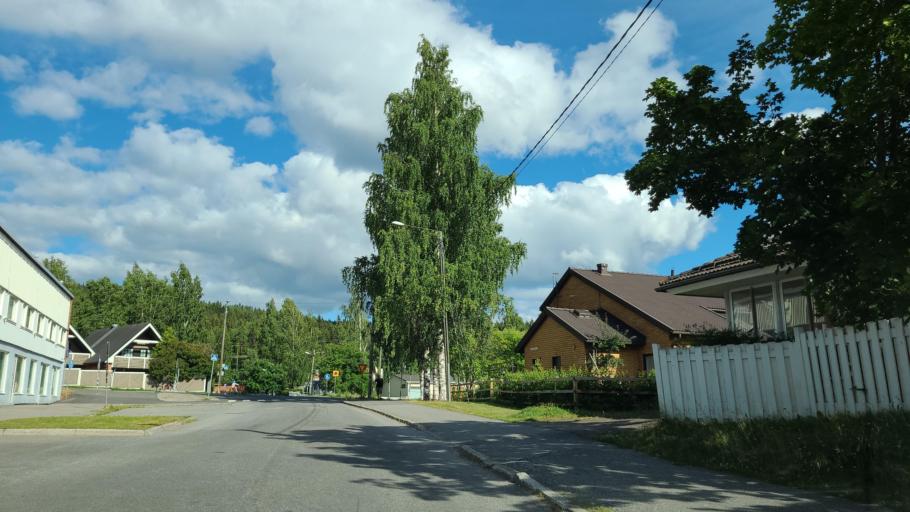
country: FI
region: Northern Savo
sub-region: Kuopio
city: Kuopio
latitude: 62.9257
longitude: 27.6309
